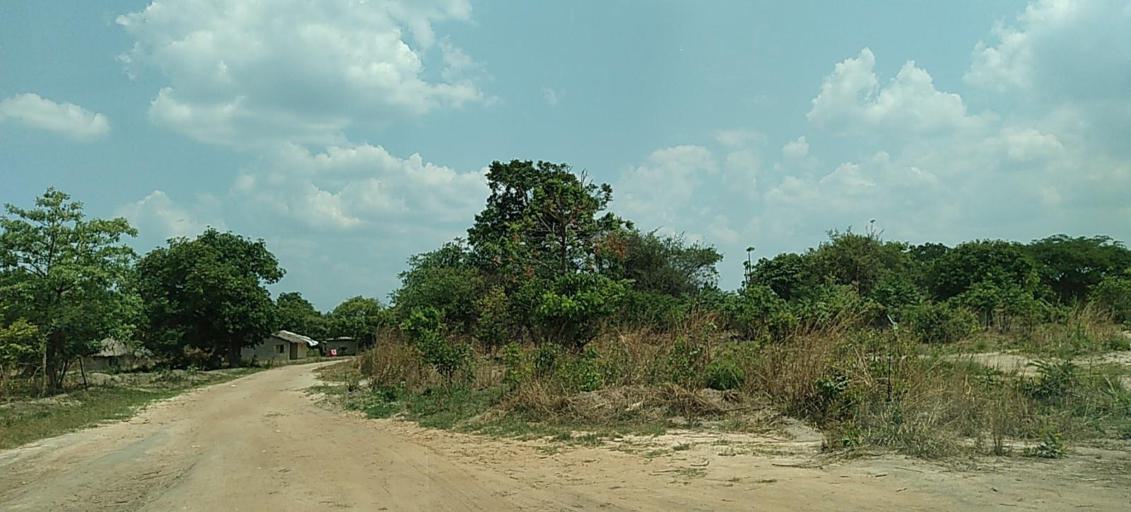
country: ZM
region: Copperbelt
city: Luanshya
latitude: -13.1540
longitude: 28.3142
